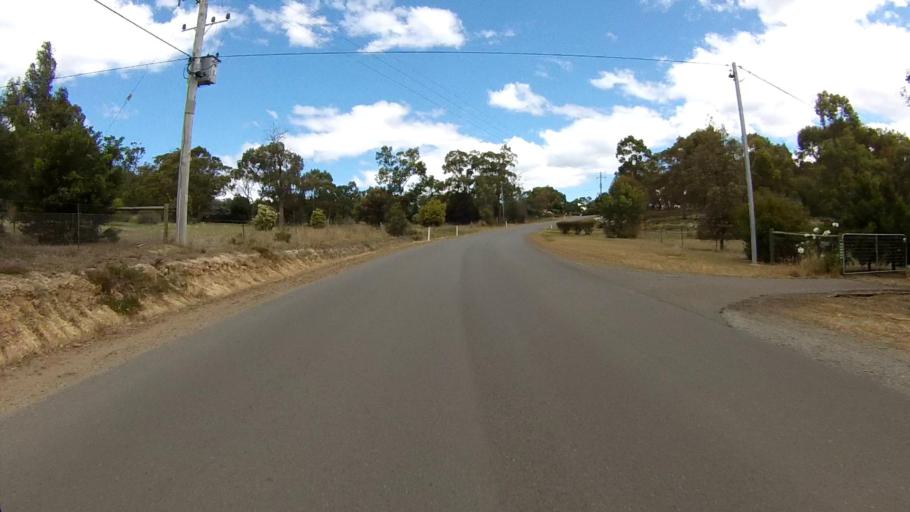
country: AU
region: Tasmania
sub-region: Clarence
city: Acton Park
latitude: -42.8717
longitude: 147.4908
